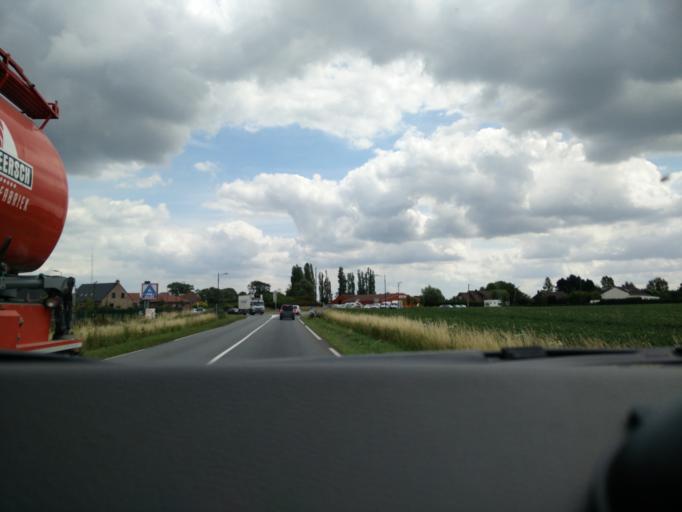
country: FR
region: Nord-Pas-de-Calais
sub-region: Departement du Nord
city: Steenvoorde
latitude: 50.8031
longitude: 2.5829
